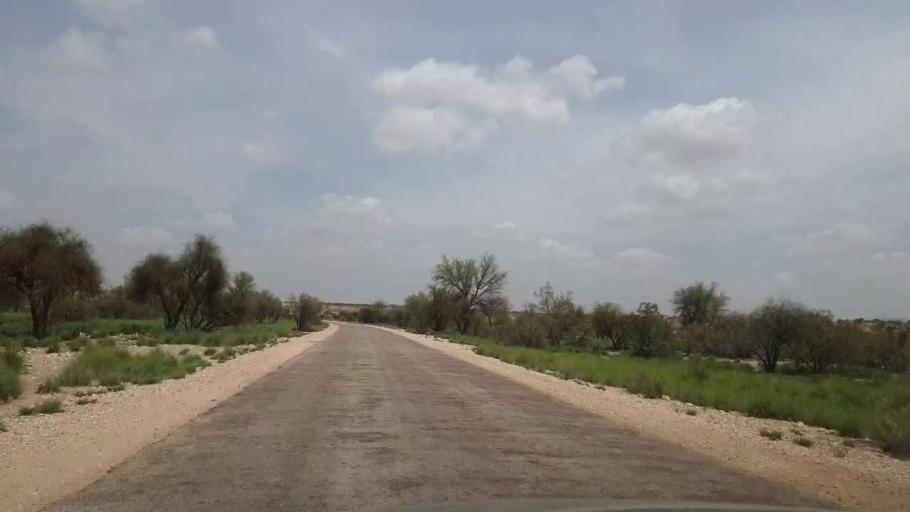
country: PK
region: Sindh
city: Kot Diji
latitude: 27.1728
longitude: 69.1961
